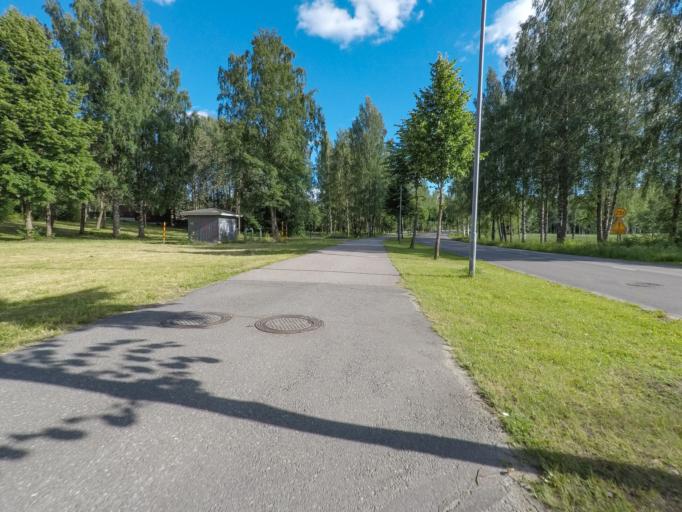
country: FI
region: South Karelia
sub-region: Lappeenranta
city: Lappeenranta
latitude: 61.0762
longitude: 28.1510
